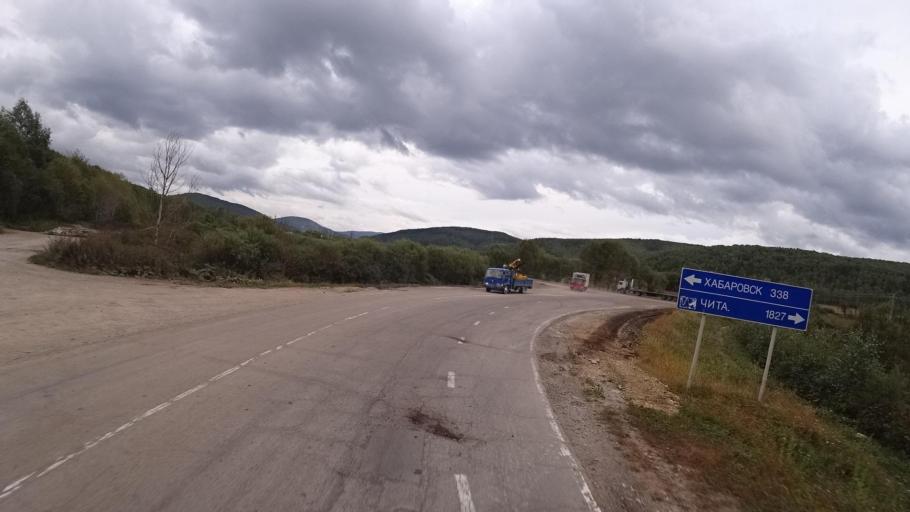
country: RU
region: Jewish Autonomous Oblast
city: Khingansk
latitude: 48.9902
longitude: 131.0792
